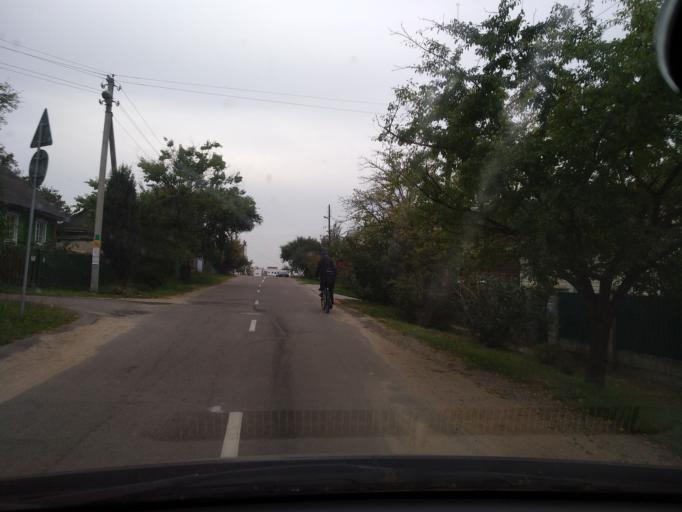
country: BY
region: Minsk
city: Minsk
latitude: 53.9396
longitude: 27.5800
